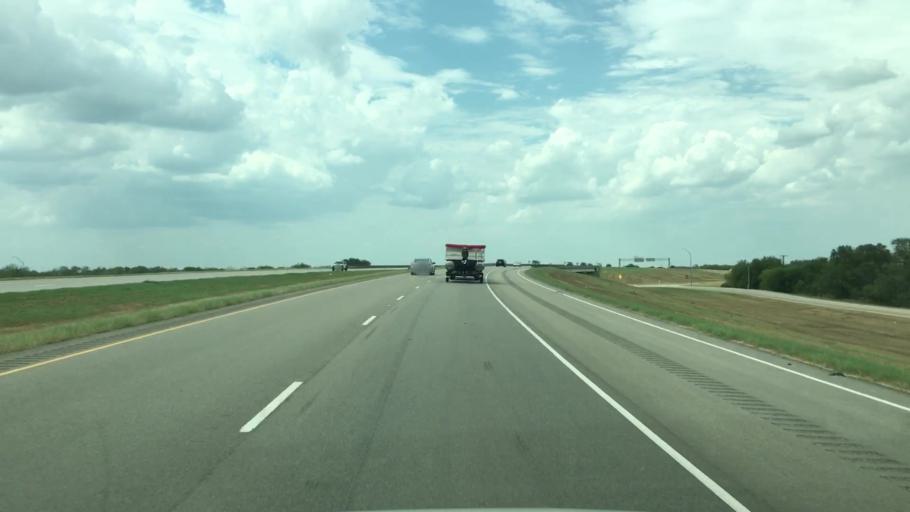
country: US
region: Texas
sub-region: Live Oak County
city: Three Rivers
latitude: 28.5237
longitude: -98.1844
